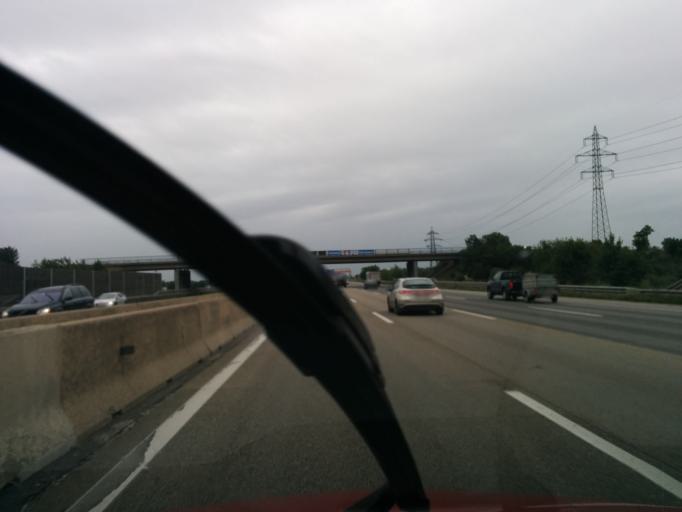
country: AT
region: Lower Austria
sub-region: Politischer Bezirk Modling
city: Laxenburg
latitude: 48.0566
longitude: 16.3407
